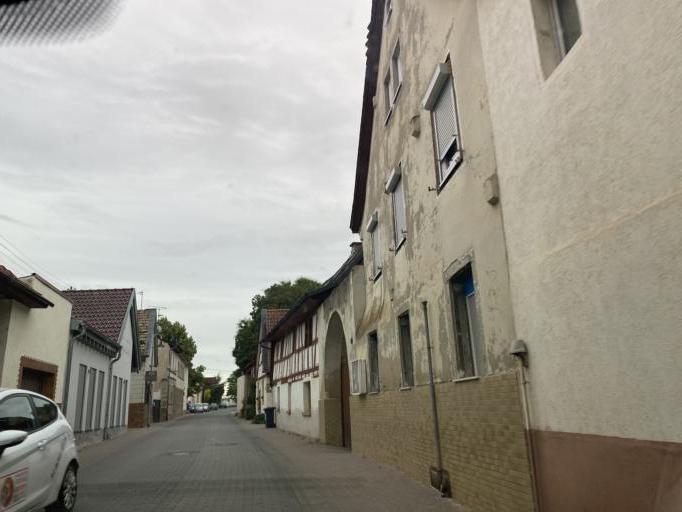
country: DE
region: Rheinland-Pfalz
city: Sprendlingen
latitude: 49.8577
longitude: 7.9890
